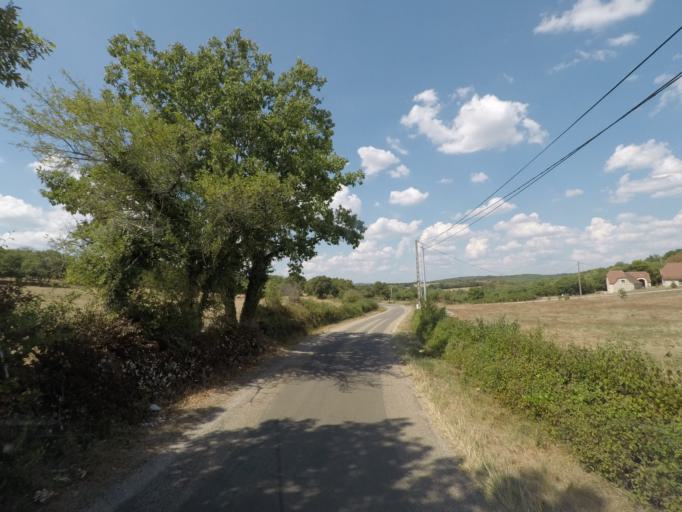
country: FR
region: Midi-Pyrenees
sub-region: Departement du Lot
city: Lalbenque
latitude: 44.5172
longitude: 1.6307
